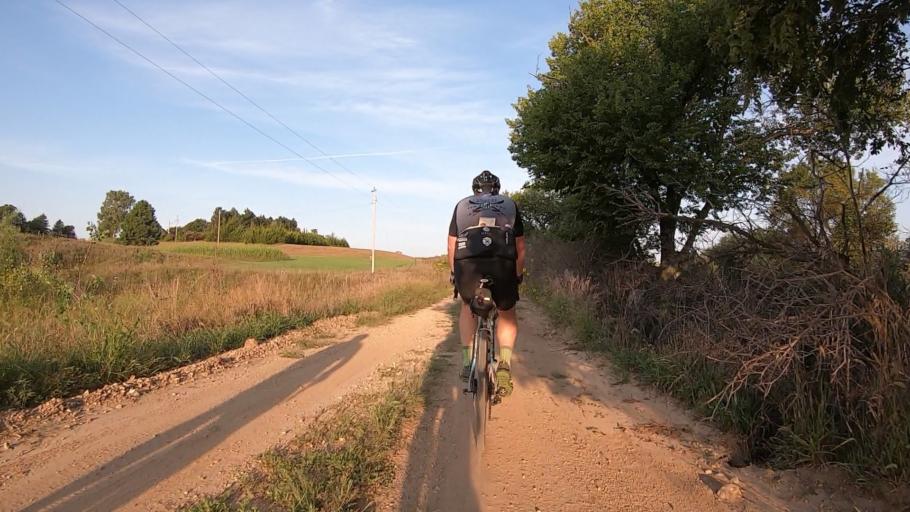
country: US
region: Kansas
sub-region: Marshall County
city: Blue Rapids
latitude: 39.7654
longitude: -96.7097
